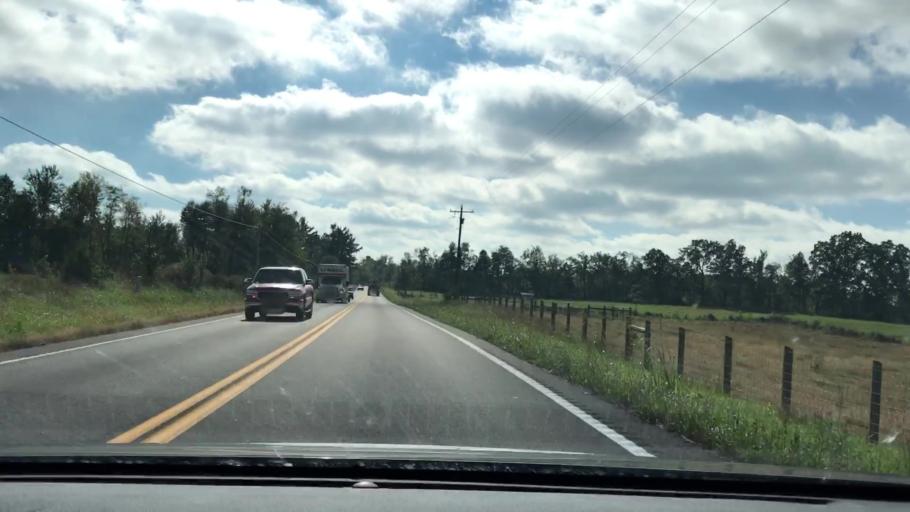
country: US
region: Tennessee
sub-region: Fentress County
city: Grimsley
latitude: 36.1796
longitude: -85.0478
